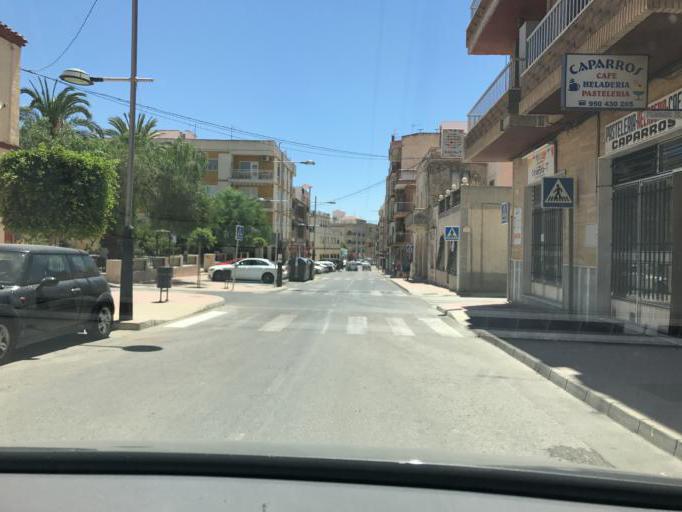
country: ES
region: Andalusia
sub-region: Provincia de Almeria
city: Albox
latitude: 37.3882
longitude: -2.1491
